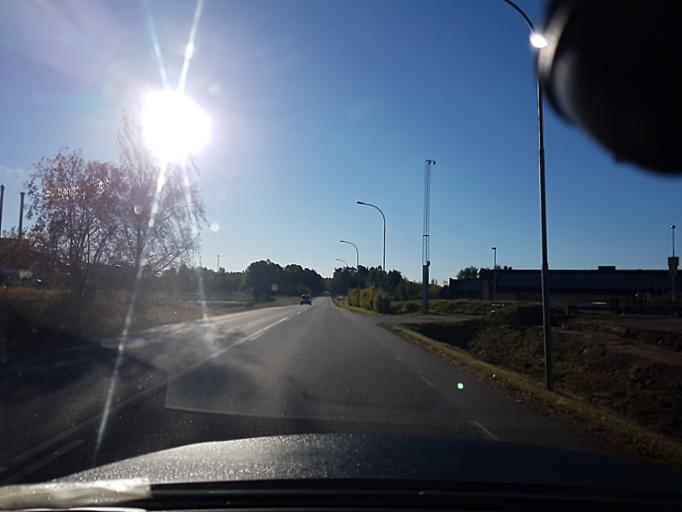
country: SE
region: Kronoberg
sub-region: Vaxjo Kommun
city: Vaexjoe
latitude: 56.8691
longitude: 14.8291
